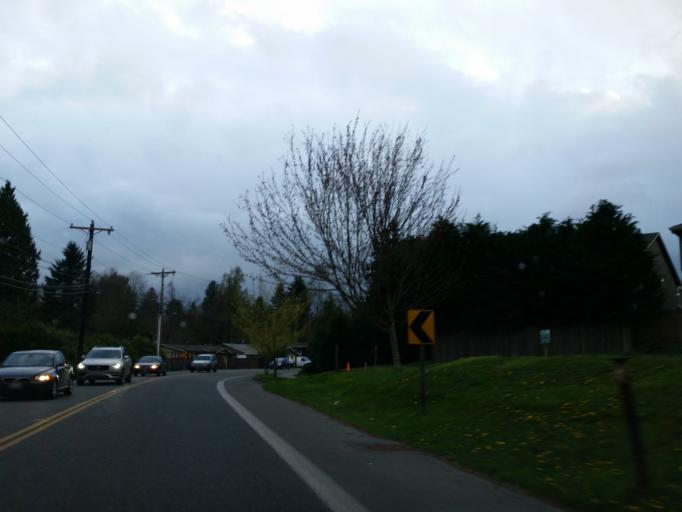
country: US
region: Washington
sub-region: Snohomish County
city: Alderwood Manor
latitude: 47.8081
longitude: -122.2772
